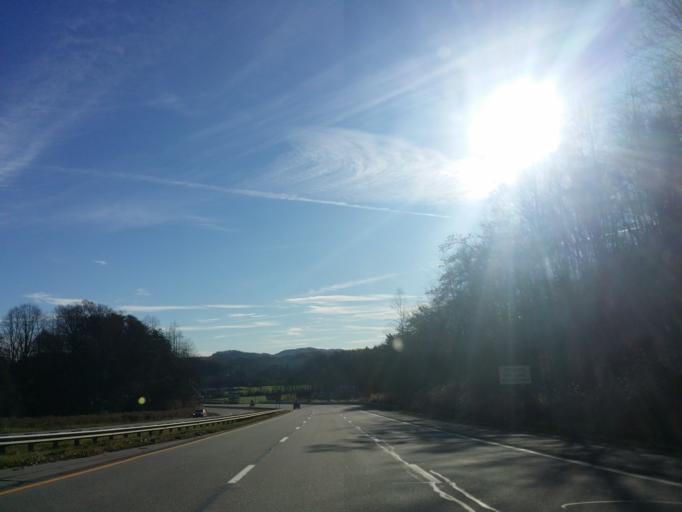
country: US
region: North Carolina
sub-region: Buncombe County
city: Black Mountain
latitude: 35.6231
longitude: -82.1939
